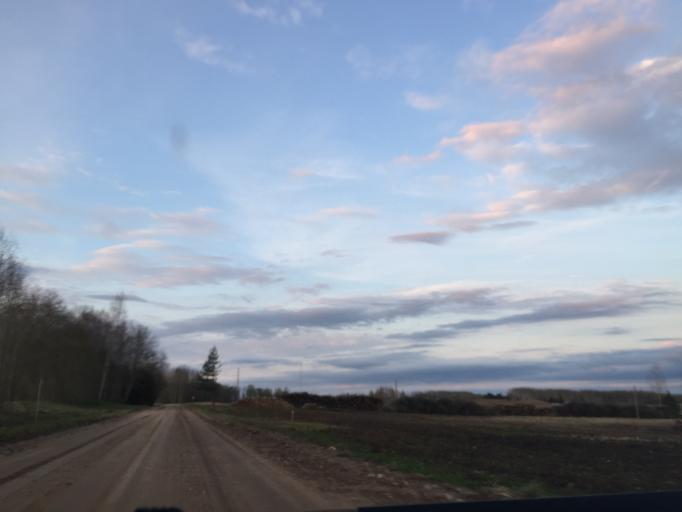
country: LV
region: Aluksnes Rajons
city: Aluksne
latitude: 57.3138
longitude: 26.9186
